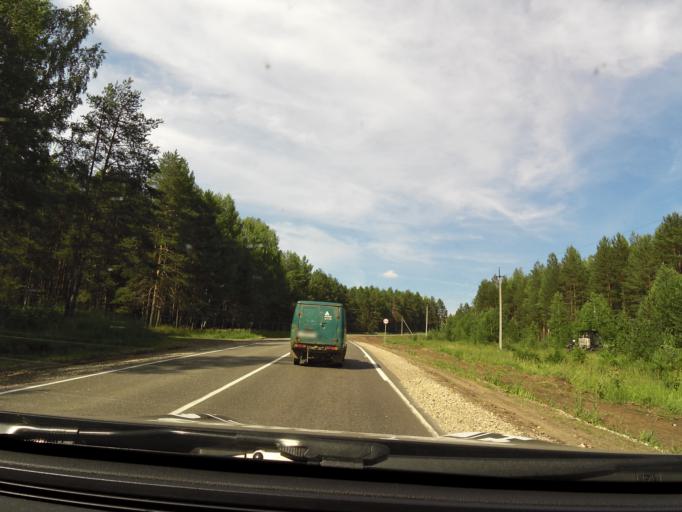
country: RU
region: Kirov
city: Belaya Kholunitsa
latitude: 58.8392
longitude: 50.6872
